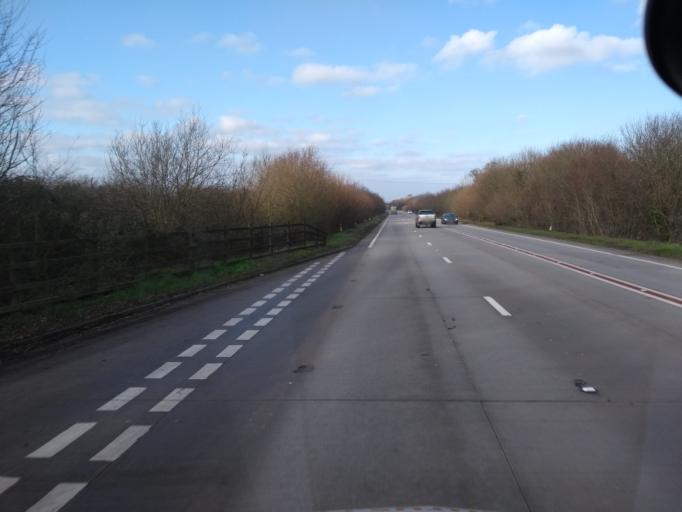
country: GB
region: England
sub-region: Somerset
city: Ilminster
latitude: 50.9375
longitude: -2.8771
